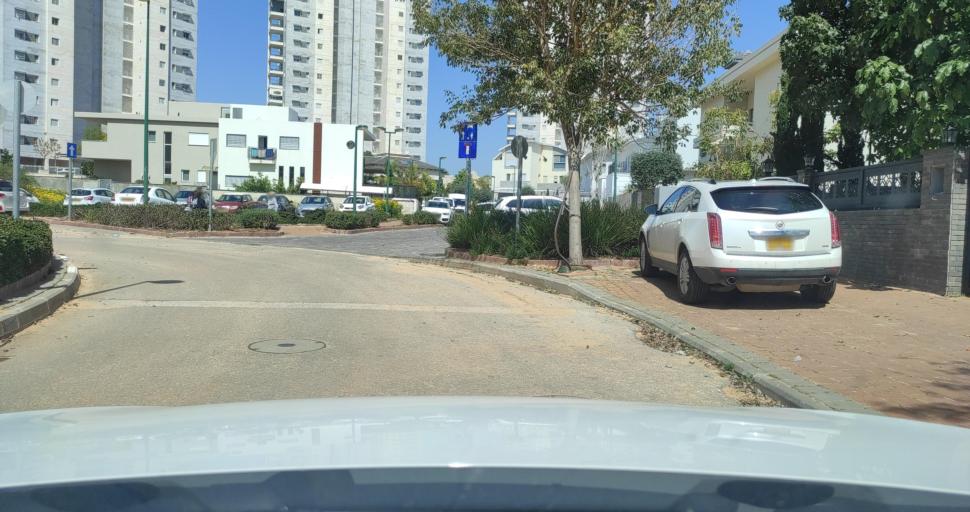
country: IL
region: Central District
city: Nordiyya
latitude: 32.3005
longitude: 34.8804
